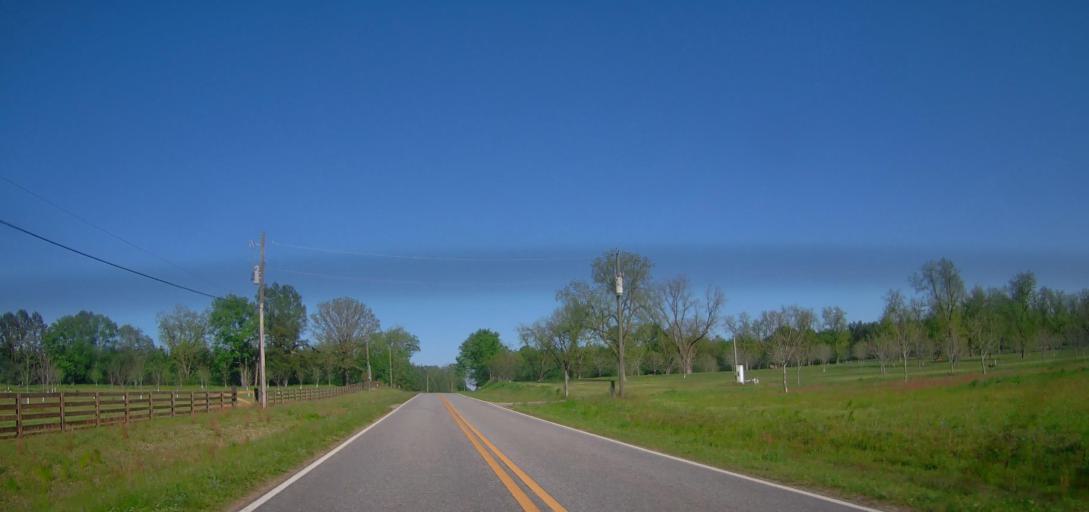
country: US
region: Georgia
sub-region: Houston County
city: Perry
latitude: 32.4516
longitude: -83.6404
